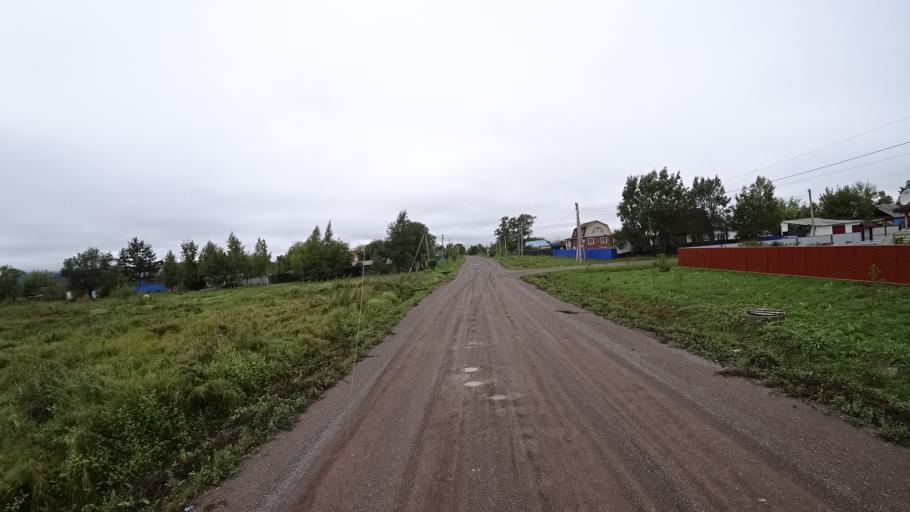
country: RU
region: Primorskiy
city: Monastyrishche
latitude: 44.1957
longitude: 132.4772
